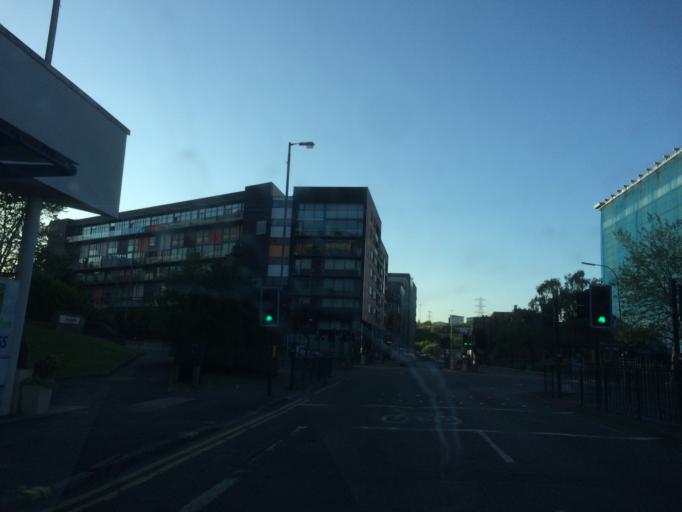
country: GB
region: Scotland
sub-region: Glasgow City
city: Glasgow
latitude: 55.8659
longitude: -4.2539
